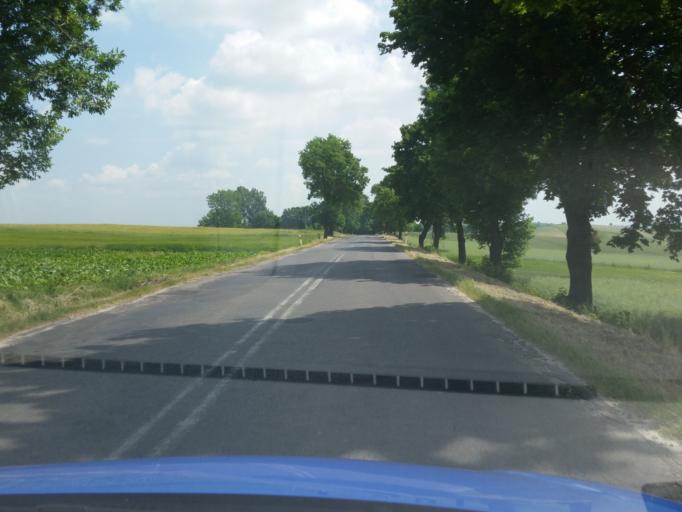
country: PL
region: Swietokrzyskie
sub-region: Powiat pinczowski
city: Dzialoszyce
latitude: 50.3238
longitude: 20.2562
